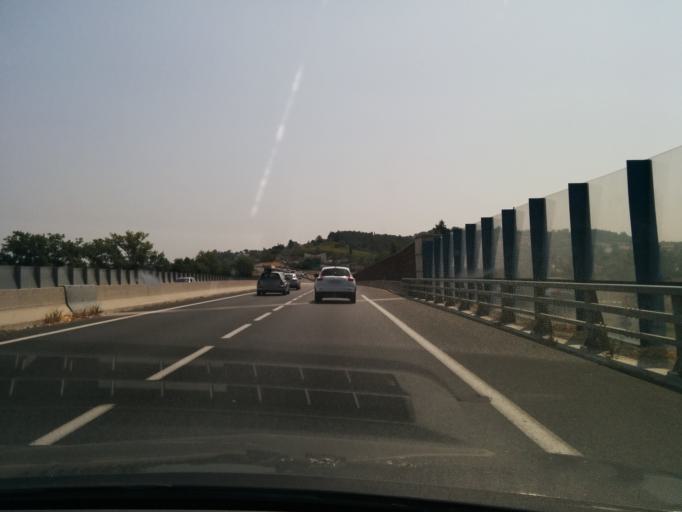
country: FR
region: Midi-Pyrenees
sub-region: Departement du Tarn
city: Le Sequestre
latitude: 43.9111
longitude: 2.1345
